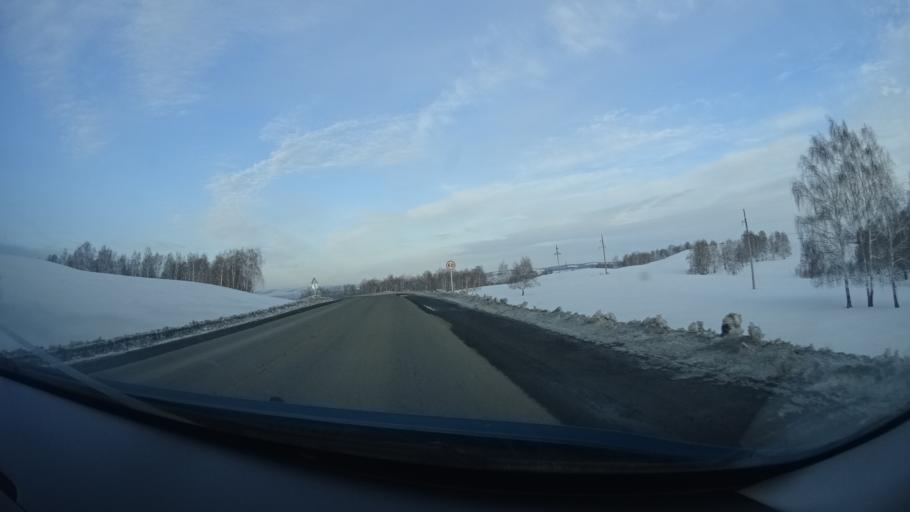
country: RU
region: Bashkortostan
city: Tubinskiy
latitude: 53.3171
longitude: 58.4971
